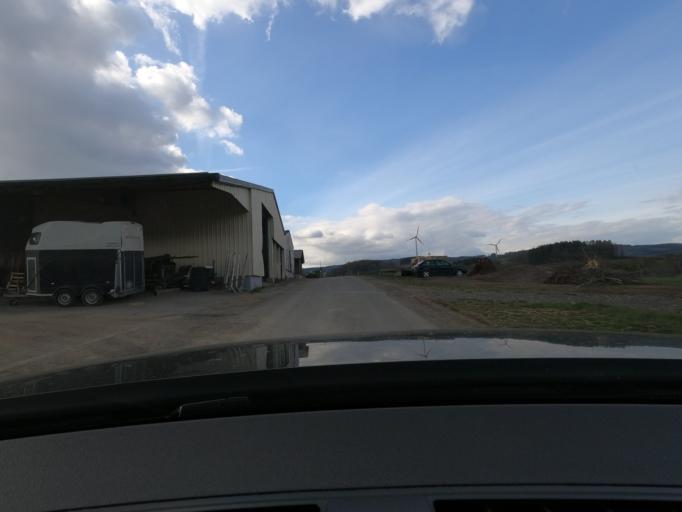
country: DE
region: North Rhine-Westphalia
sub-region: Regierungsbezirk Arnsberg
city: Herscheid
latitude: 51.1119
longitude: 7.7835
